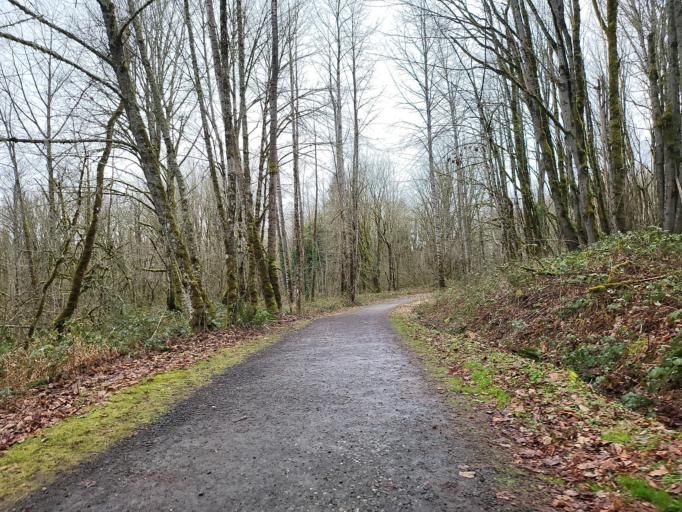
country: US
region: Washington
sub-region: King County
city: Newcastle
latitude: 47.5308
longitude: -122.1236
